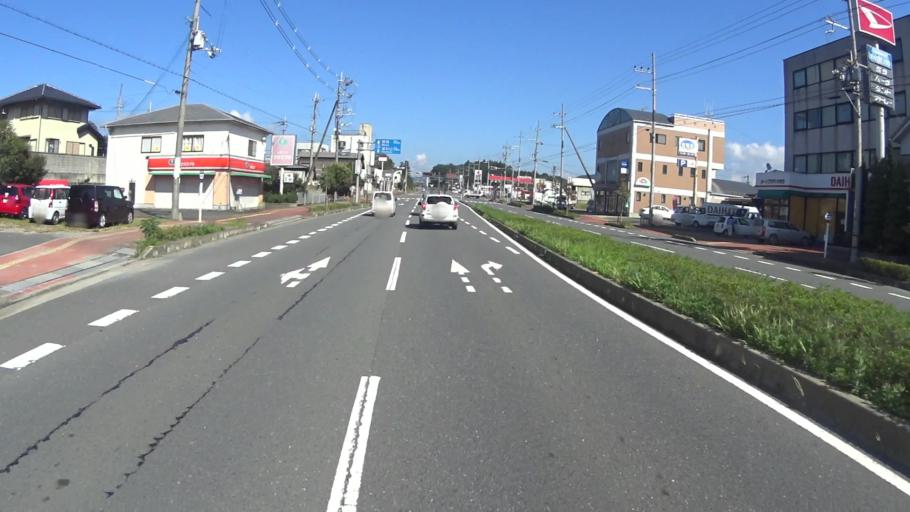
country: JP
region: Kyoto
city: Kameoka
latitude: 35.1595
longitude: 135.4259
